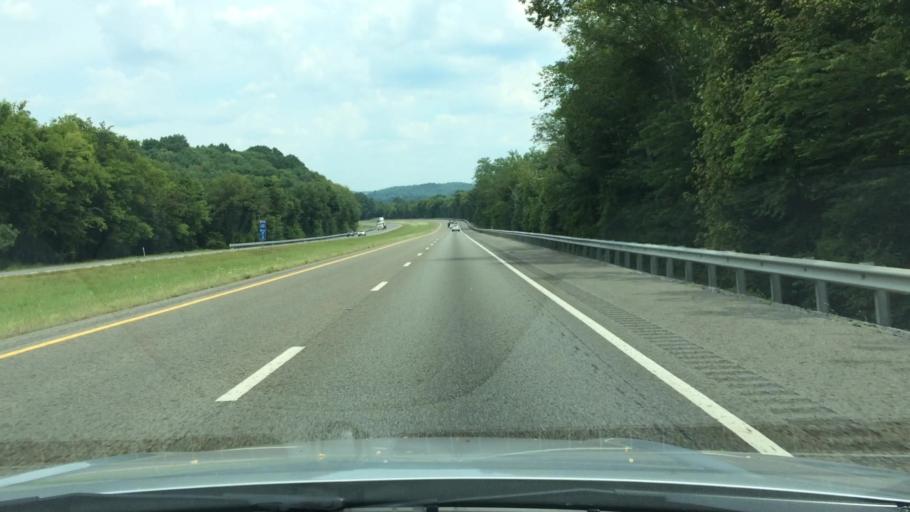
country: US
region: Tennessee
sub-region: Marshall County
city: Cornersville
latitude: 35.4099
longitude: -86.8785
